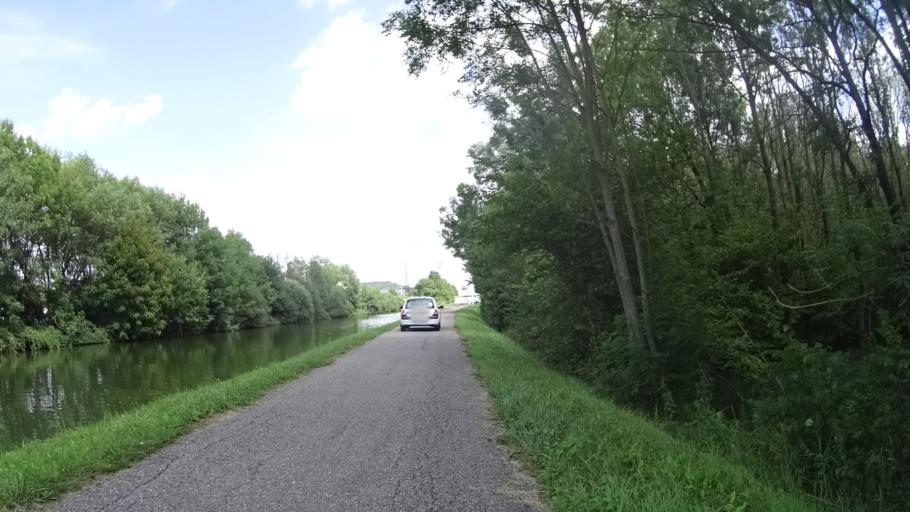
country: FR
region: Lorraine
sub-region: Departement de Meurthe-et-Moselle
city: Foug
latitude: 48.6766
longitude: 5.7950
